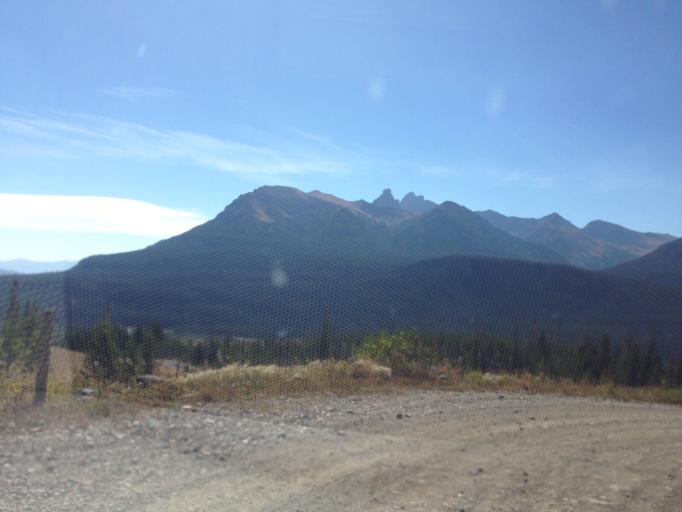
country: US
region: Montana
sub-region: Stillwater County
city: Absarokee
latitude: 45.0369
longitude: -109.9115
